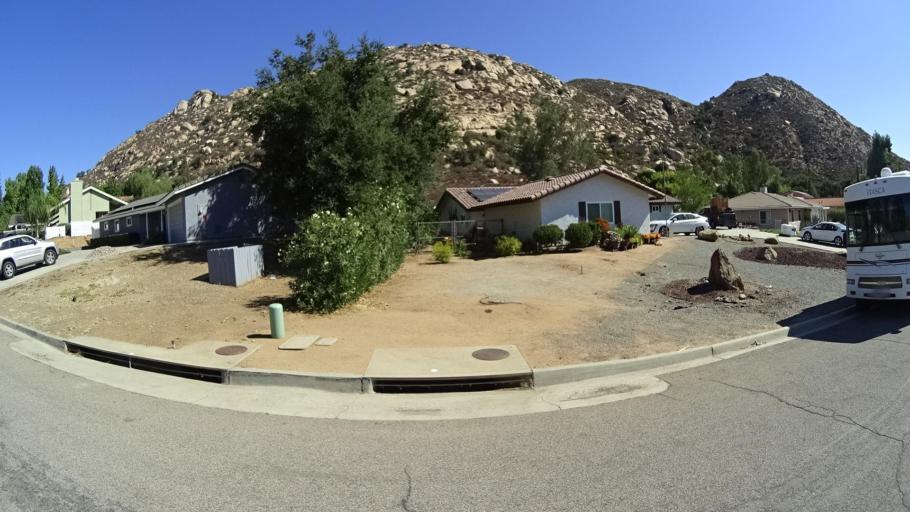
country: US
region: California
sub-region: San Diego County
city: San Diego Country Estates
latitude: 33.0084
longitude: -116.7838
